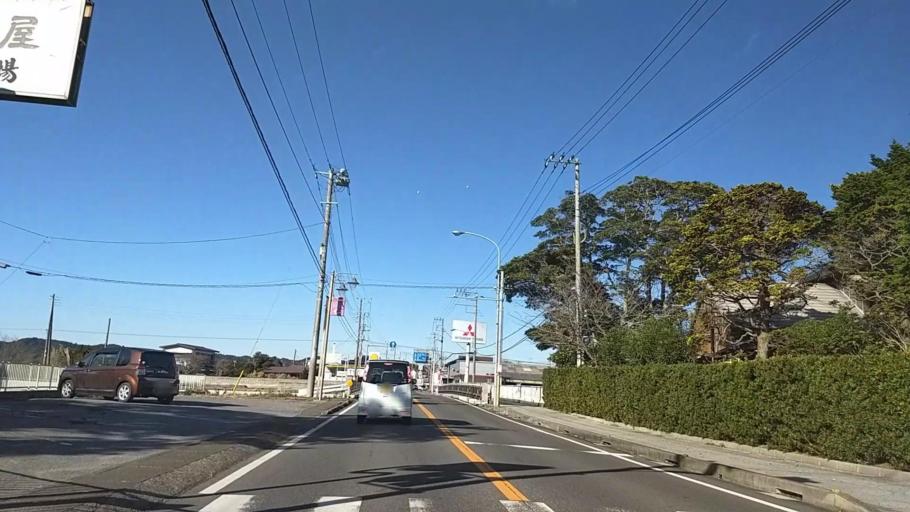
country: JP
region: Chiba
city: Ohara
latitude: 35.2558
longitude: 140.3945
